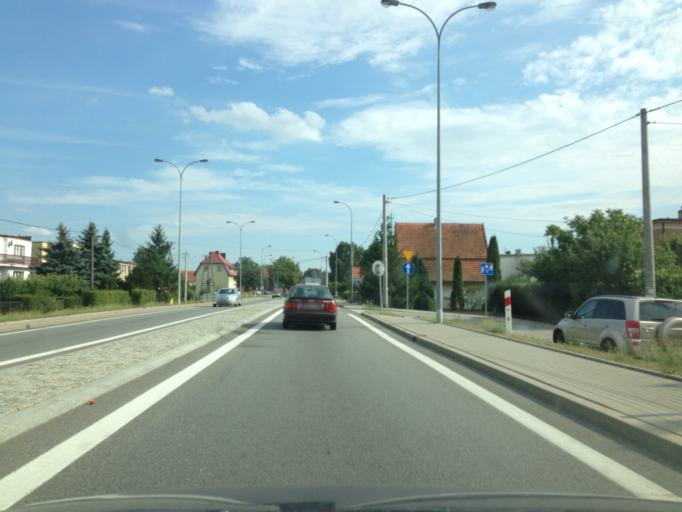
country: PL
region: Pomeranian Voivodeship
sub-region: Powiat gdanski
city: Pszczolki
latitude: 54.1758
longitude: 18.6900
